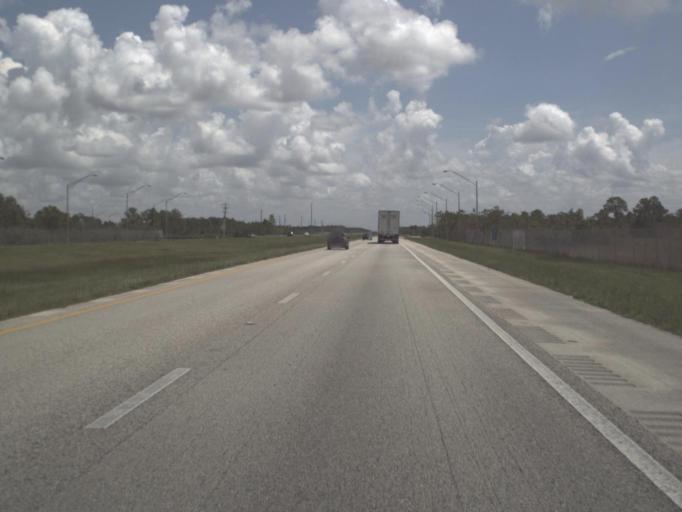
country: US
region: Florida
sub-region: Collier County
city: Immokalee
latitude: 26.1668
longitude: -81.2033
